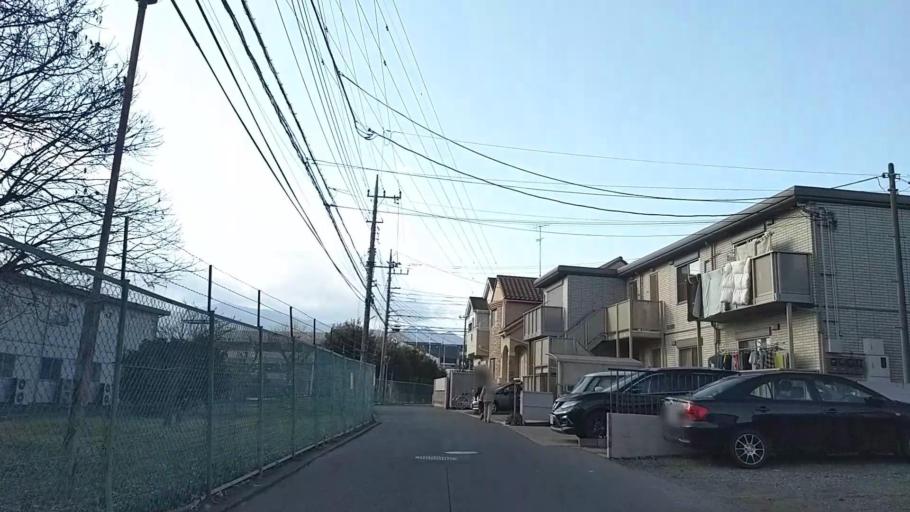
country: JP
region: Kanagawa
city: Atsugi
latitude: 35.4496
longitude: 139.3447
